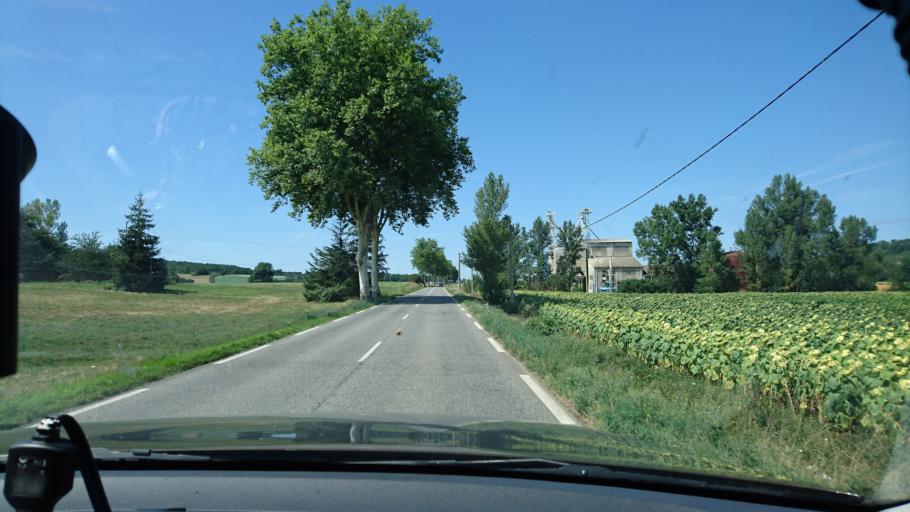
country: FR
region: Midi-Pyrenees
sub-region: Departement de l'Ariege
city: Lezat-sur-Leze
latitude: 43.2366
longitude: 1.3721
